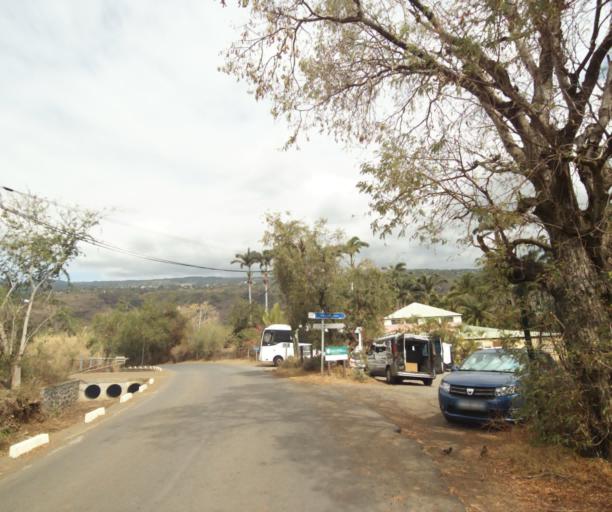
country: RE
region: Reunion
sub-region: Reunion
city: Saint-Paul
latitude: -20.9902
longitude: 55.3017
